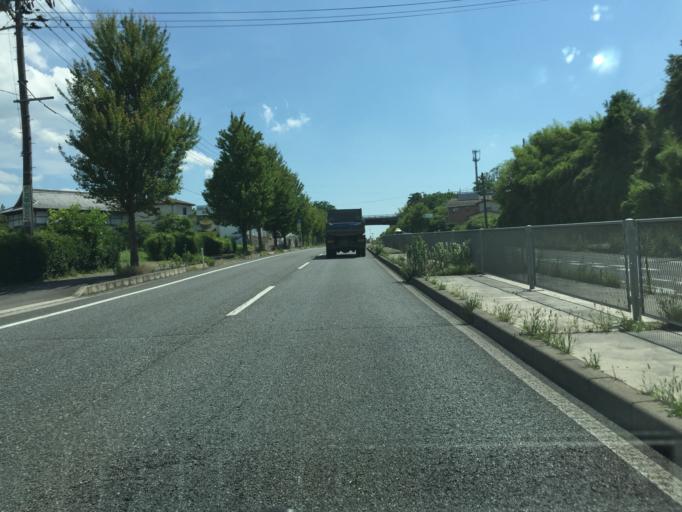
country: JP
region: Fukushima
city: Motomiya
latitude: 37.5088
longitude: 140.3951
